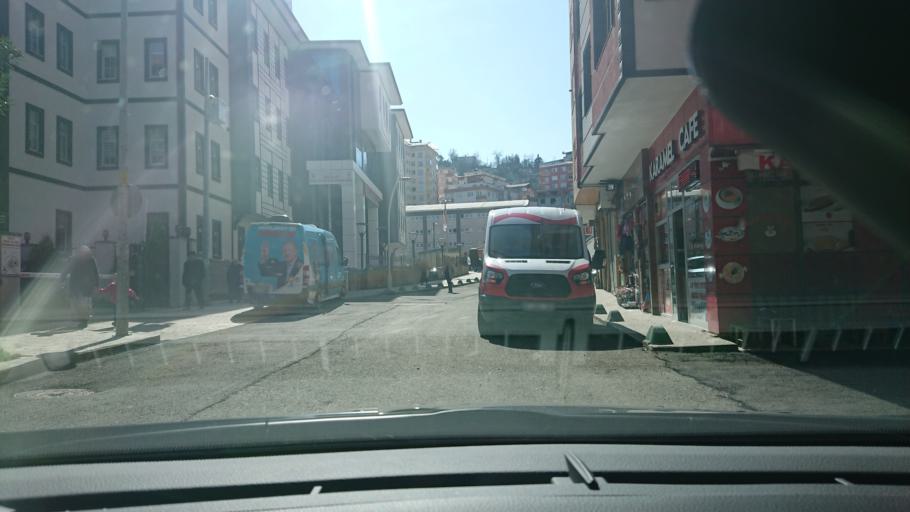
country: TR
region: Rize
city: Rize
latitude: 41.0227
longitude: 40.5284
